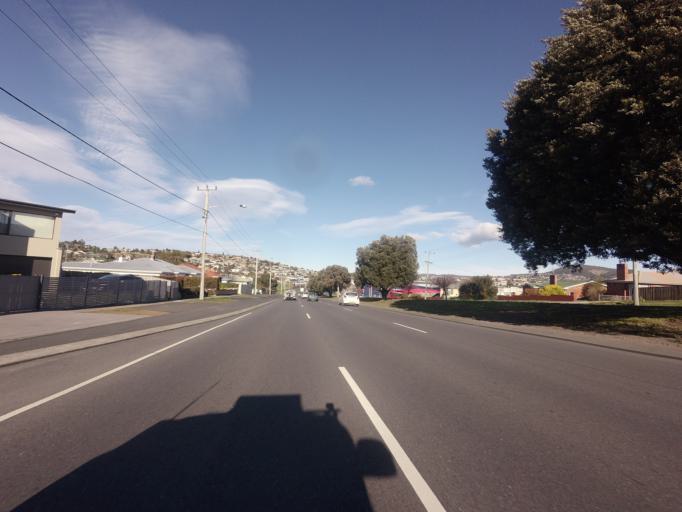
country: AU
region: Tasmania
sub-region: Glenorchy
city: Goodwood
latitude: -42.8345
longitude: 147.2996
